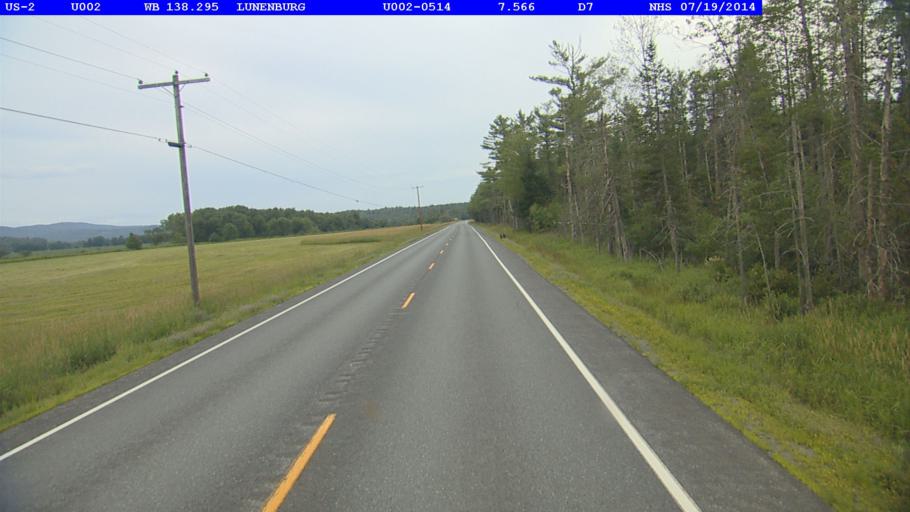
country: US
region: New Hampshire
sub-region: Coos County
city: Lancaster
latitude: 44.4815
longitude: -71.6370
